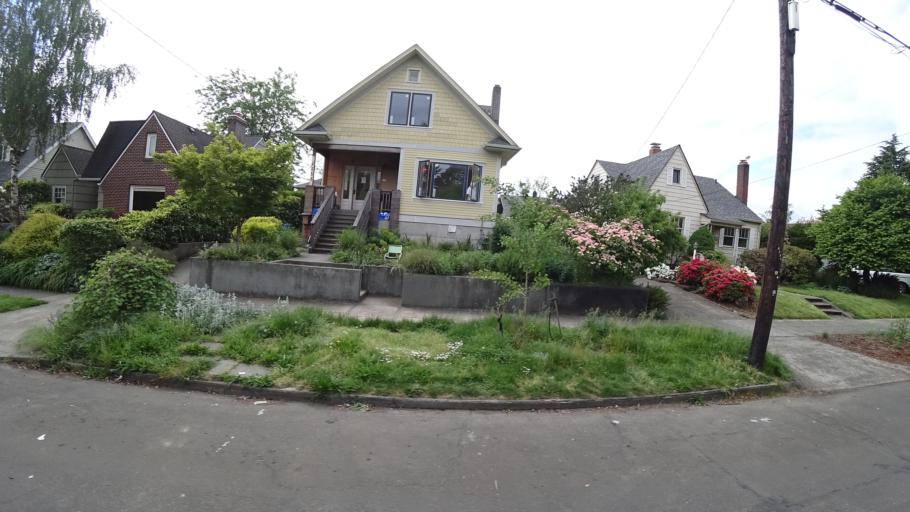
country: US
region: Oregon
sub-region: Multnomah County
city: Lents
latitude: 45.5075
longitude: -122.6028
